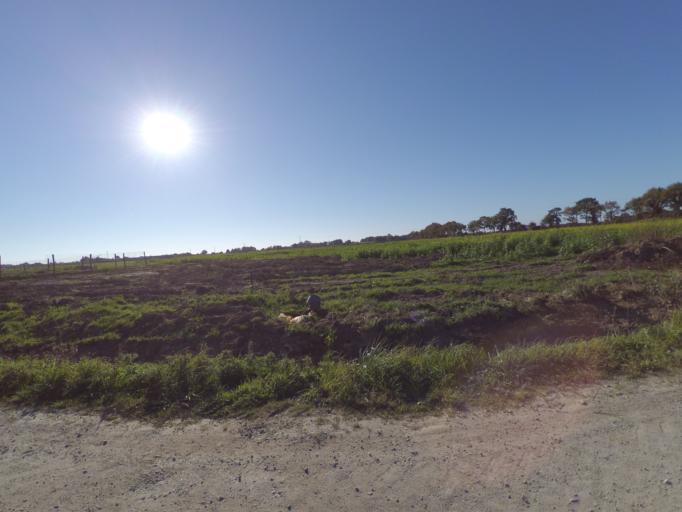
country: FR
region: Pays de la Loire
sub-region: Departement de la Loire-Atlantique
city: Remouille
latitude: 47.0140
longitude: -1.3857
